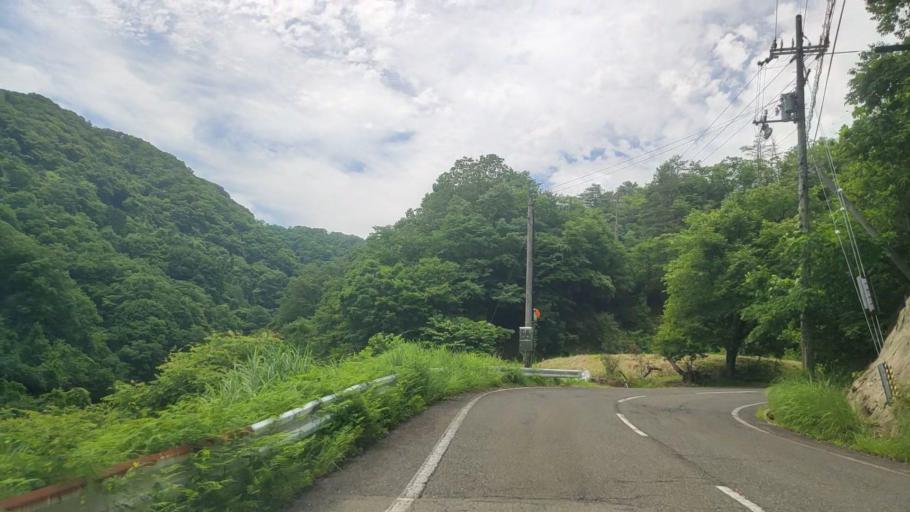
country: JP
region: Hyogo
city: Toyooka
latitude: 35.5214
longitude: 134.6956
